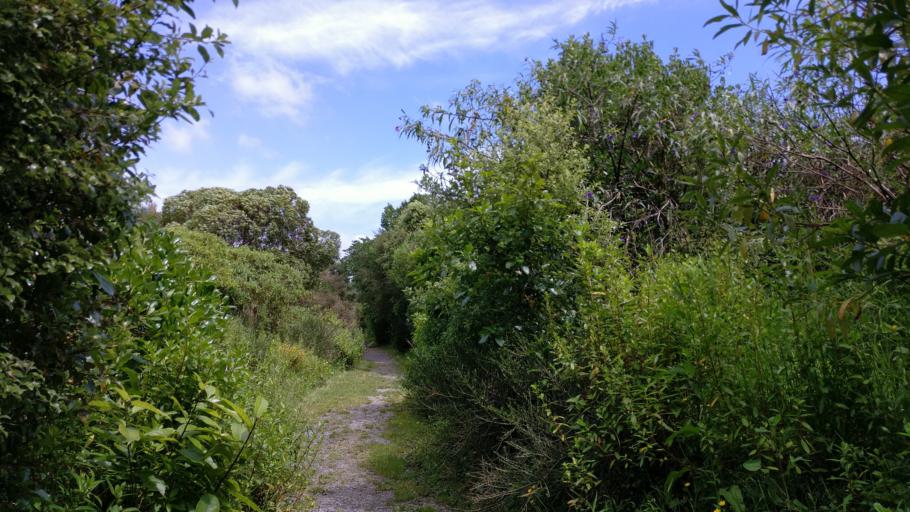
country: NZ
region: Wellington
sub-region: Porirua City
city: Porirua
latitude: -41.1031
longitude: 174.9164
